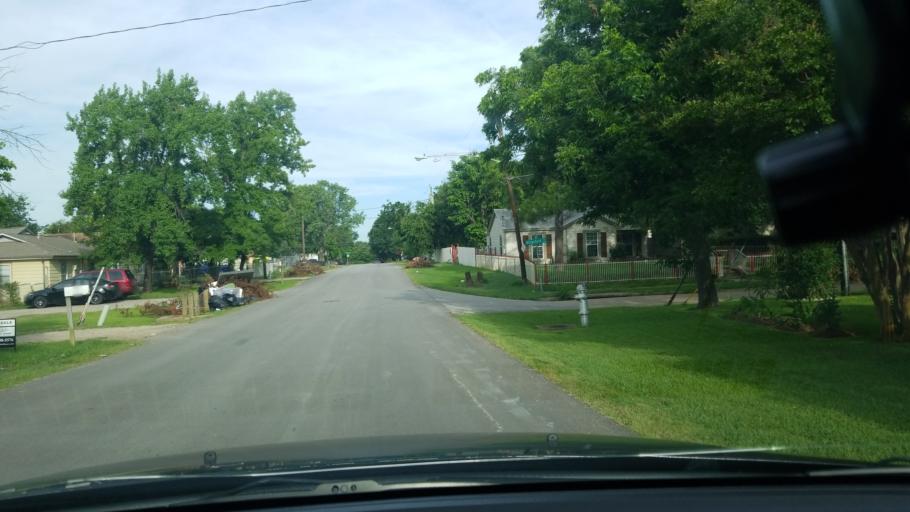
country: US
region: Texas
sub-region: Dallas County
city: Balch Springs
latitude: 32.7593
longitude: -96.6637
